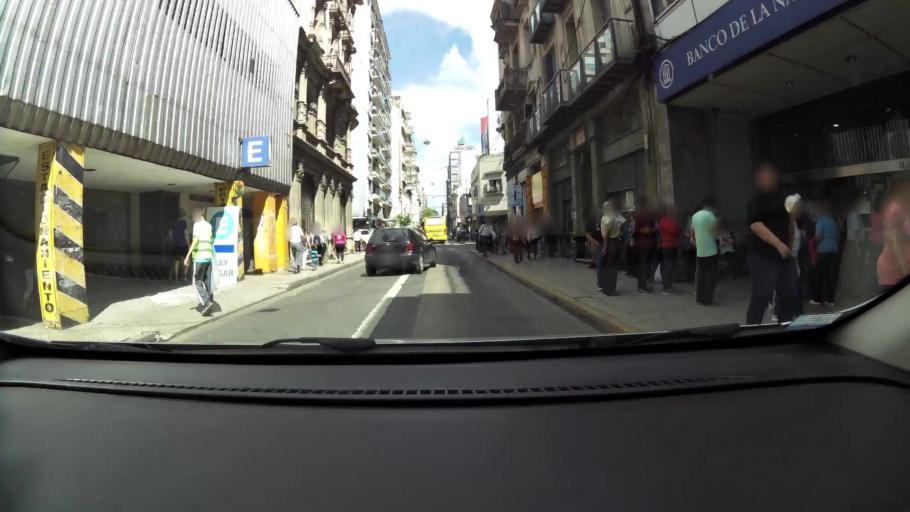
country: AR
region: Santa Fe
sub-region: Departamento de Rosario
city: Rosario
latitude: -32.9447
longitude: -60.6402
